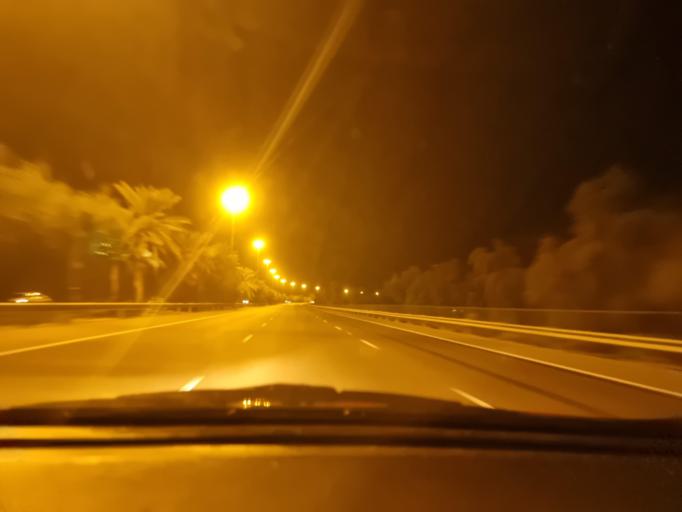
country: AE
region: Abu Dhabi
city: Al Ain
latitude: 24.1689
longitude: 55.2783
